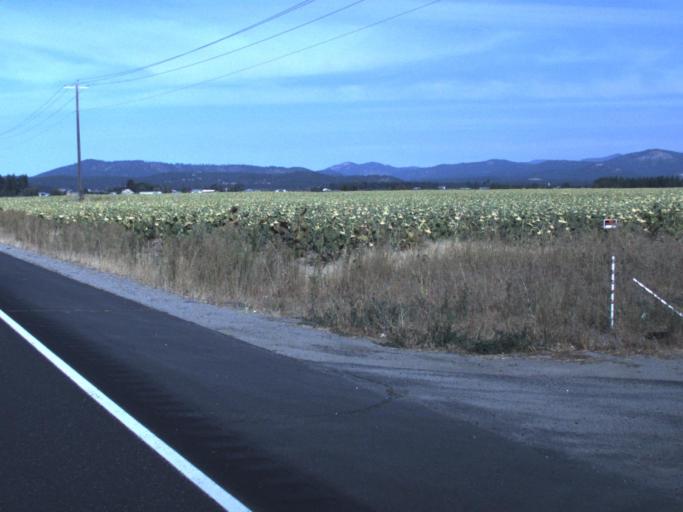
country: US
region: Washington
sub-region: Spokane County
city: Deer Park
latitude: 47.9640
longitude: -117.5021
